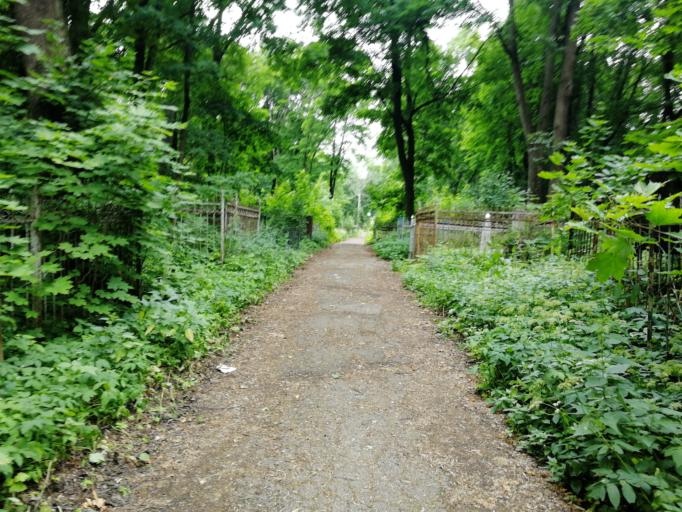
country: RU
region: Tula
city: Tula
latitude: 54.1789
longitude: 37.6127
